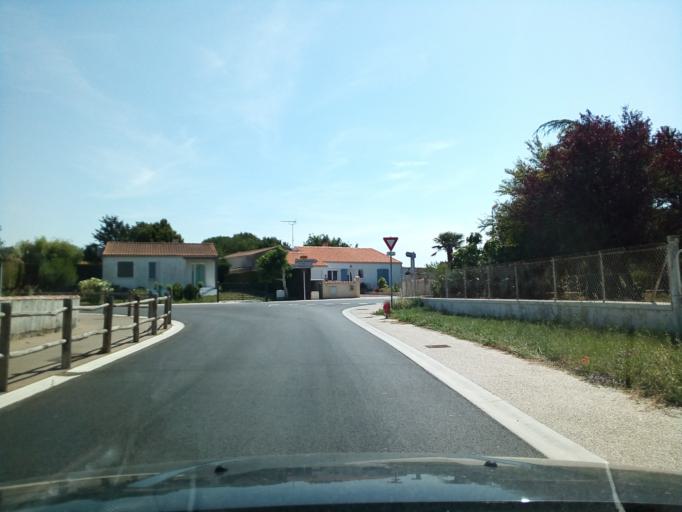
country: FR
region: Poitou-Charentes
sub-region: Departement de la Charente-Maritime
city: Boyard-Ville
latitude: 45.9744
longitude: -1.2988
